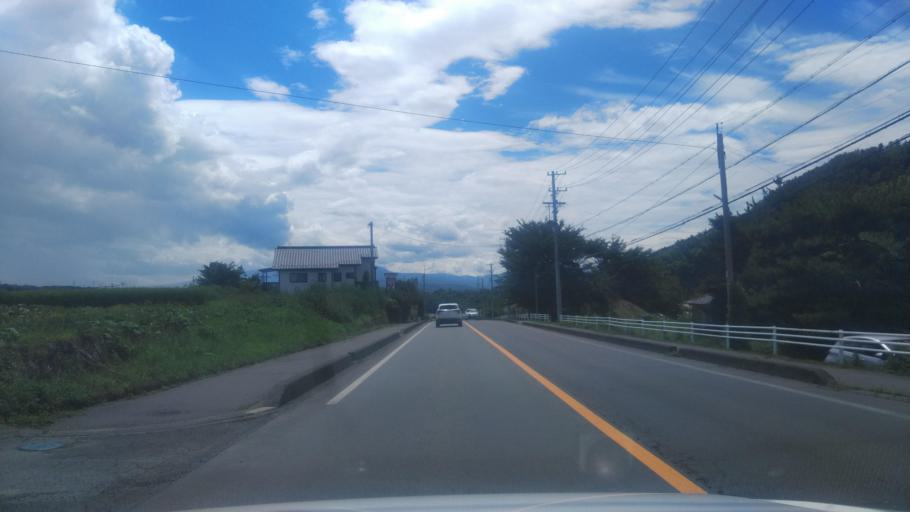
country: JP
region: Nagano
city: Ueda
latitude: 36.4306
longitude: 138.2984
